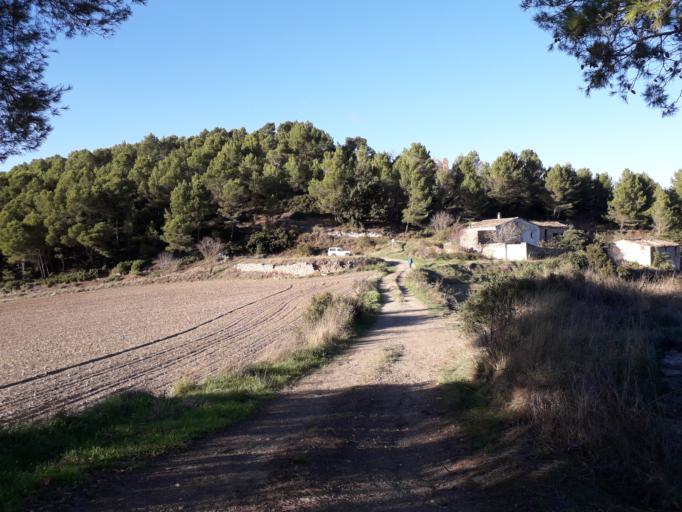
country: ES
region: Catalonia
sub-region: Provincia de Barcelona
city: Bellprat
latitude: 41.5605
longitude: 1.4509
